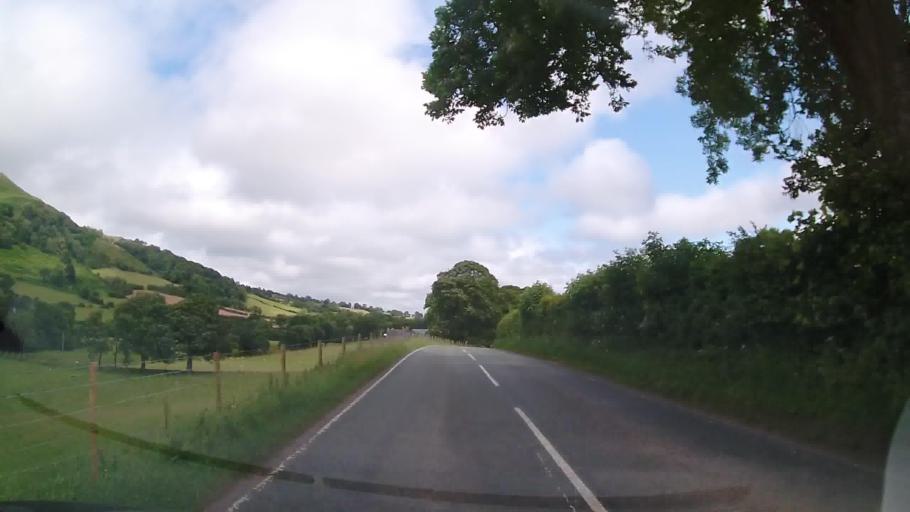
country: GB
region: Wales
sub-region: Sir Powys
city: Llangynog
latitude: 52.8214
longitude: -3.3834
